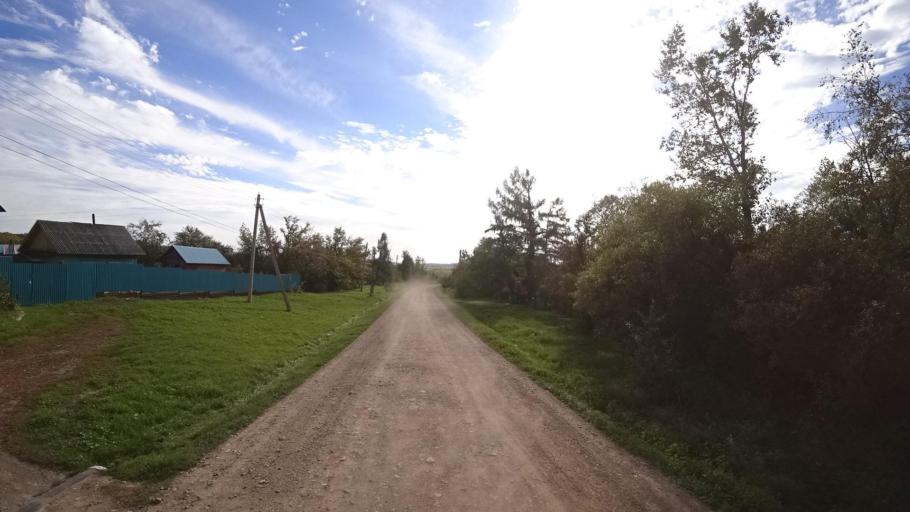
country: RU
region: Primorskiy
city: Dostoyevka
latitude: 44.2973
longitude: 133.4505
